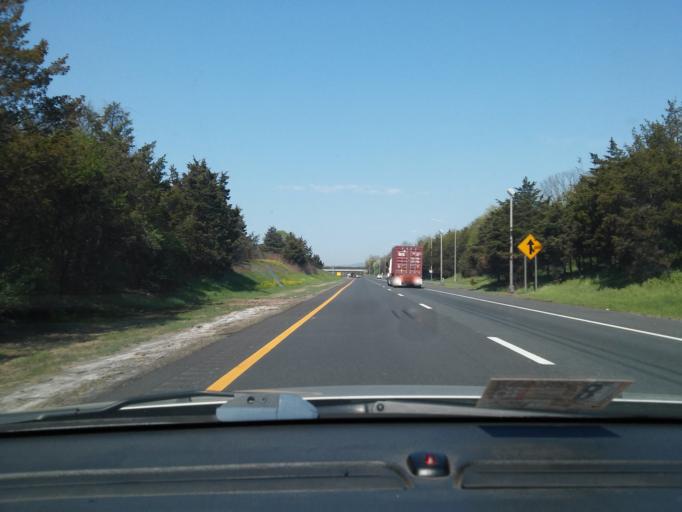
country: US
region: New Jersey
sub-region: Somerset County
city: Bedminster
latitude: 40.6432
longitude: -74.6488
